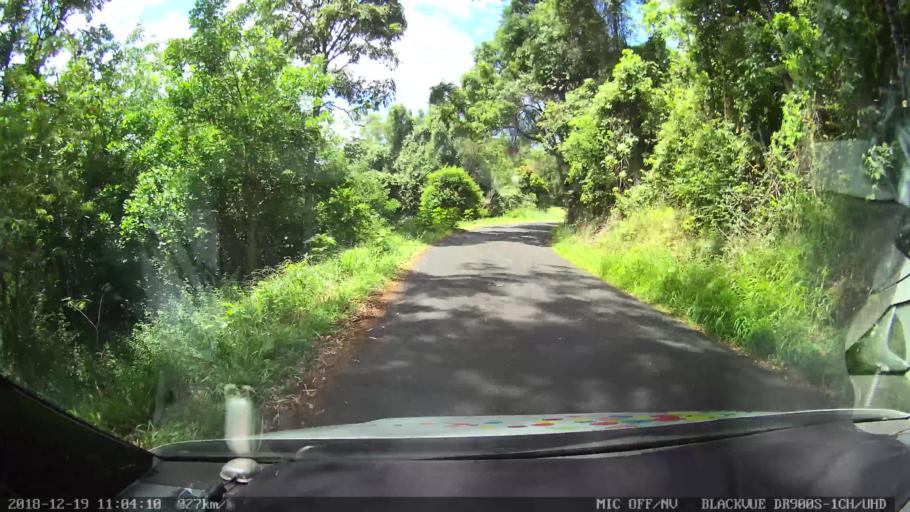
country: AU
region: New South Wales
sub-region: Lismore Municipality
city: Nimbin
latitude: -28.6136
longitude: 153.2679
